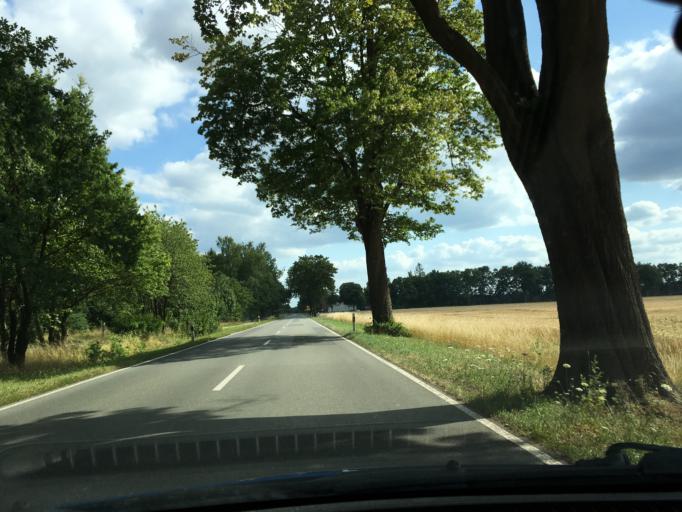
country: DE
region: Mecklenburg-Vorpommern
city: Lubtheen
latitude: 53.3239
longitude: 11.0755
